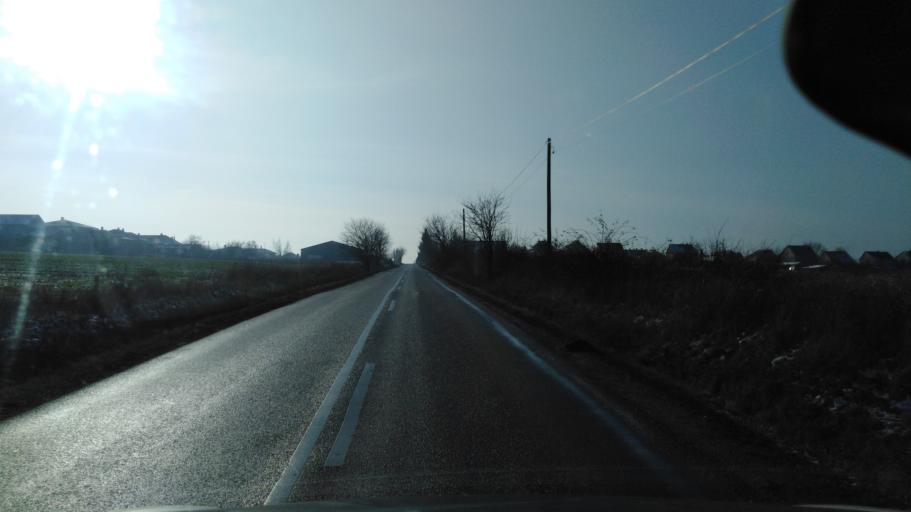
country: HU
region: Nograd
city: Paszto
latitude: 47.9344
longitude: 19.7050
